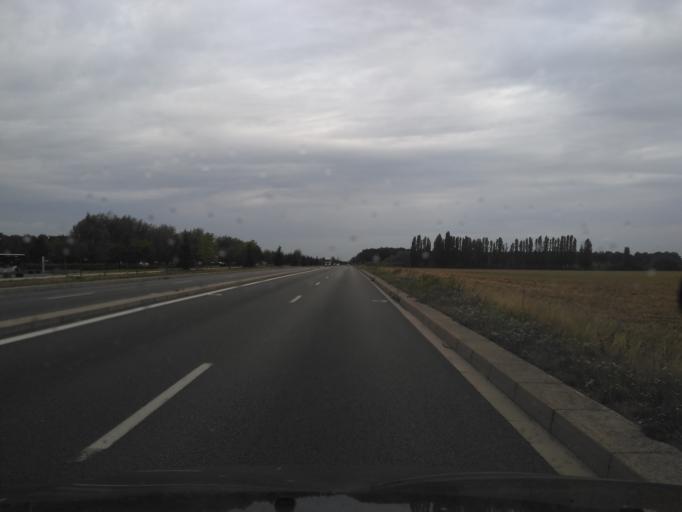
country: FR
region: Ile-de-France
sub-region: Departement de Seine-et-Marne
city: Vert-Saint-Denis
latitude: 48.5846
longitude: 2.6072
